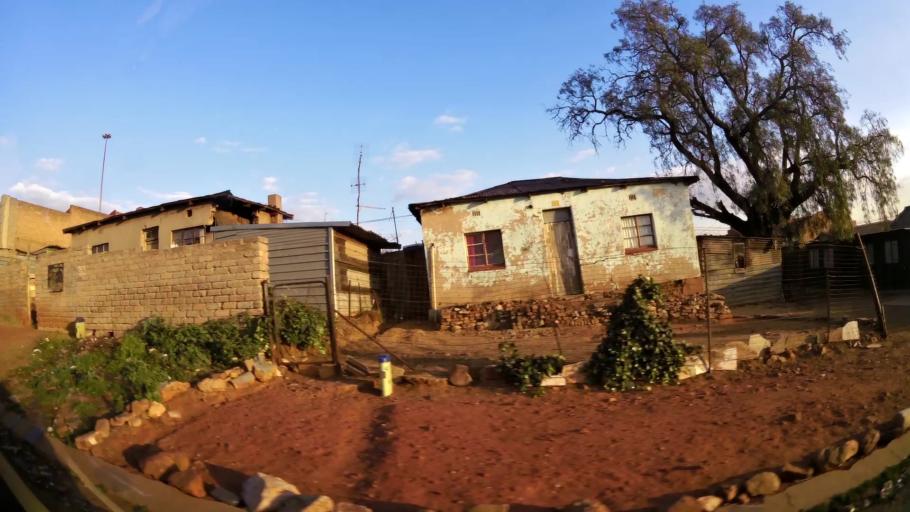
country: ZA
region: Gauteng
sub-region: West Rand District Municipality
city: Krugersdorp
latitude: -26.0714
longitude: 27.7557
